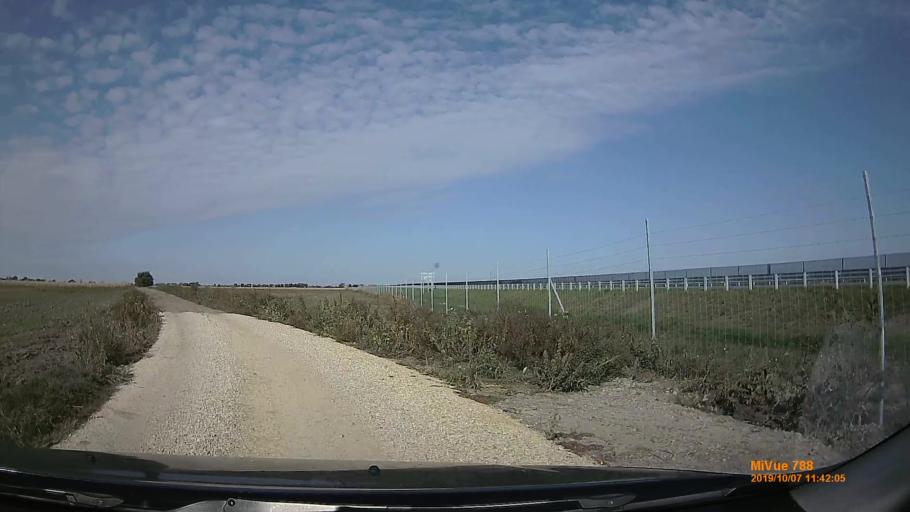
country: HU
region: Bekes
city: Kondoros
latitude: 46.7978
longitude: 20.6999
